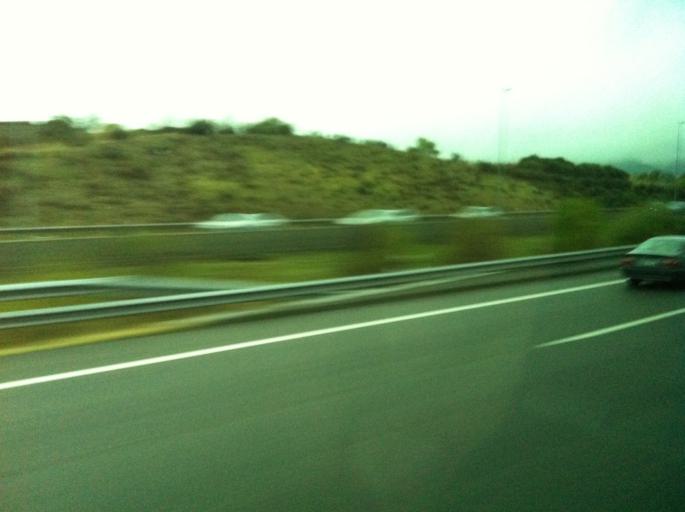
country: ES
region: Madrid
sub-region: Provincia de Madrid
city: Guadarrama
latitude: 40.6531
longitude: -4.0812
